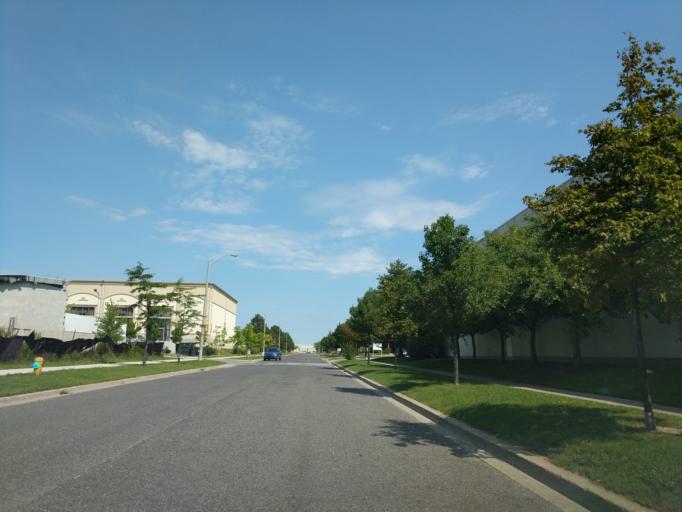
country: CA
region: Ontario
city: Markham
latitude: 43.8249
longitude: -79.2461
